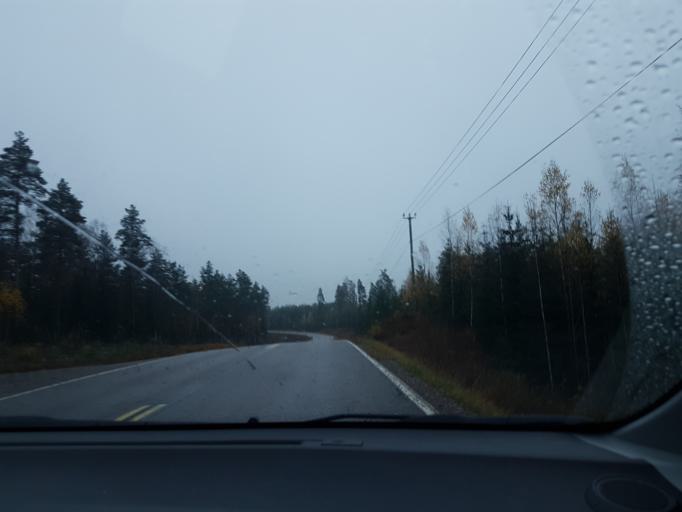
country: FI
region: Uusimaa
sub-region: Helsinki
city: Maentsaelae
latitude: 60.5885
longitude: 25.1837
